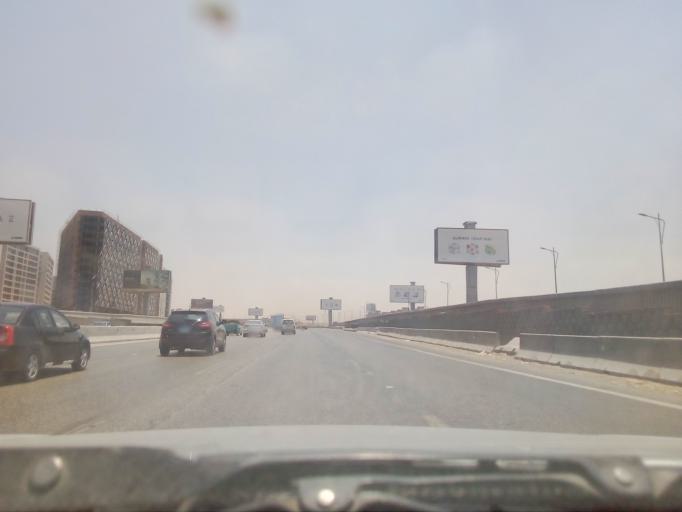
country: EG
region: Al Jizah
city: Al Hawamidiyah
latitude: 29.9797
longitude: 31.3518
